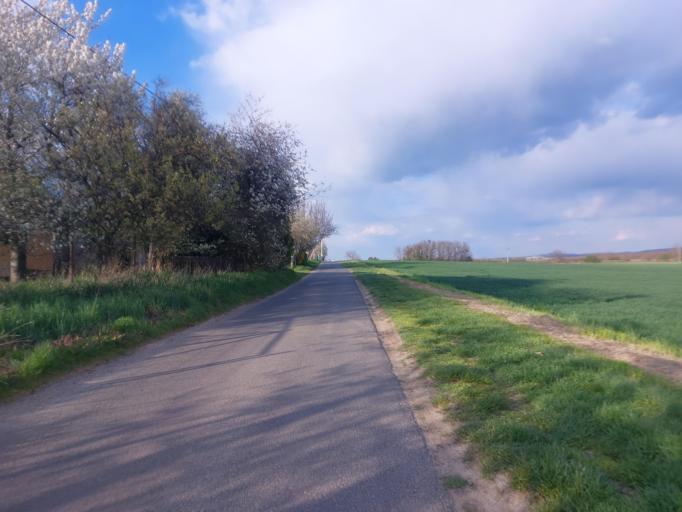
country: HU
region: Veszprem
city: Devecser
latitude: 47.1410
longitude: 17.3878
